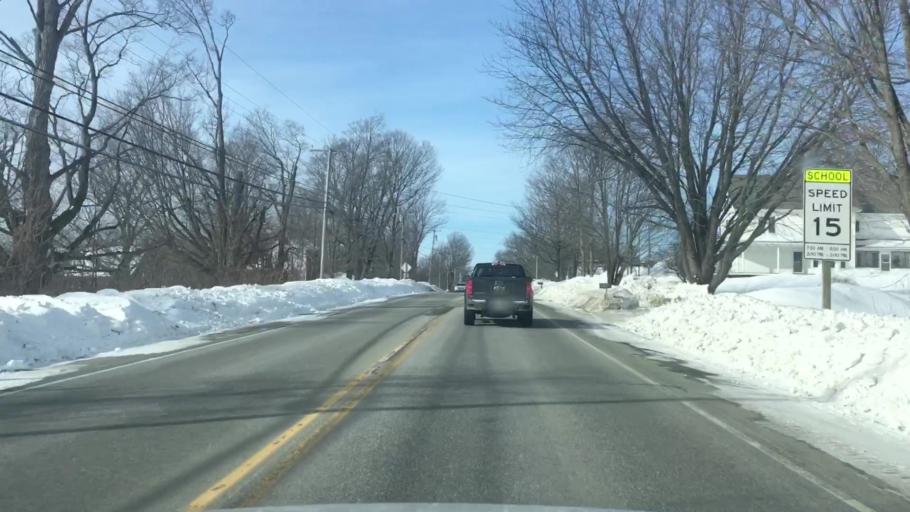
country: US
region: Maine
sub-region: Penobscot County
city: Charleston
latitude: 44.9951
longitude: -69.0195
